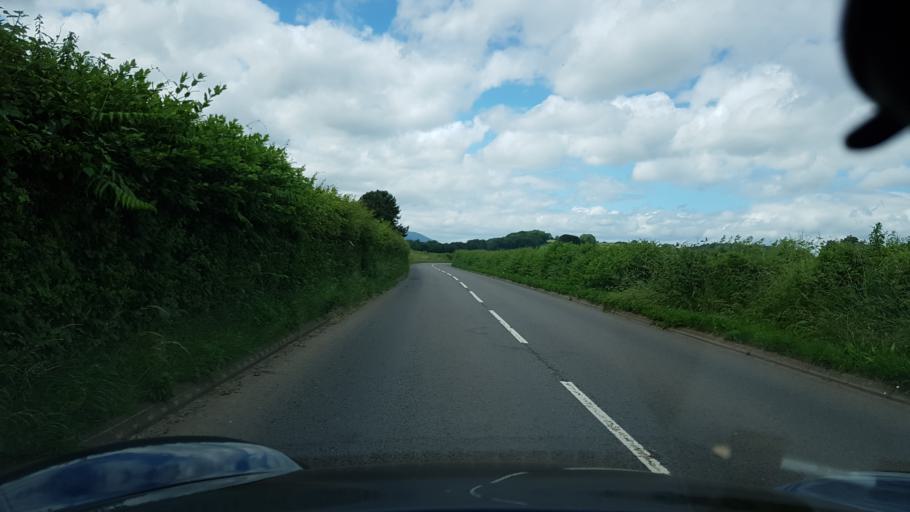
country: GB
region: Wales
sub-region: Monmouthshire
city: Usk
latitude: 51.7242
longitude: -2.9179
